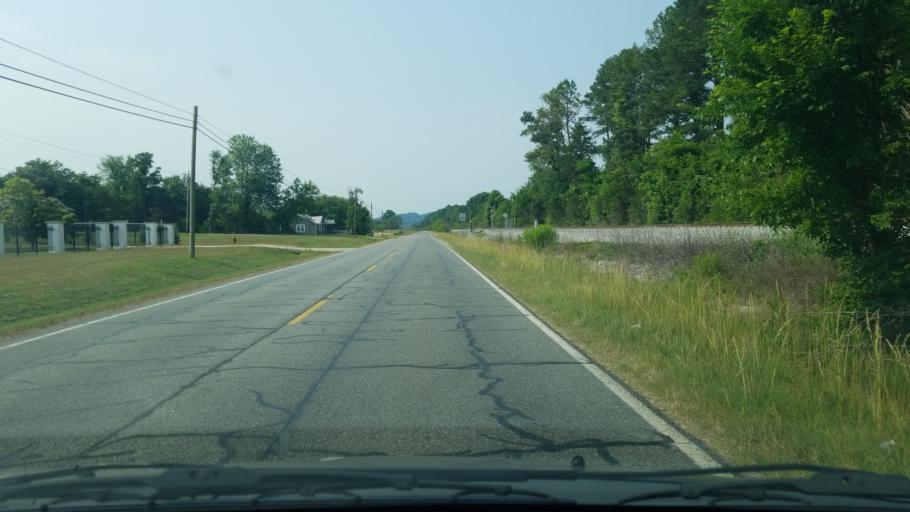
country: US
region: Georgia
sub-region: Catoosa County
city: Ringgold
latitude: 34.9514
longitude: -85.1041
